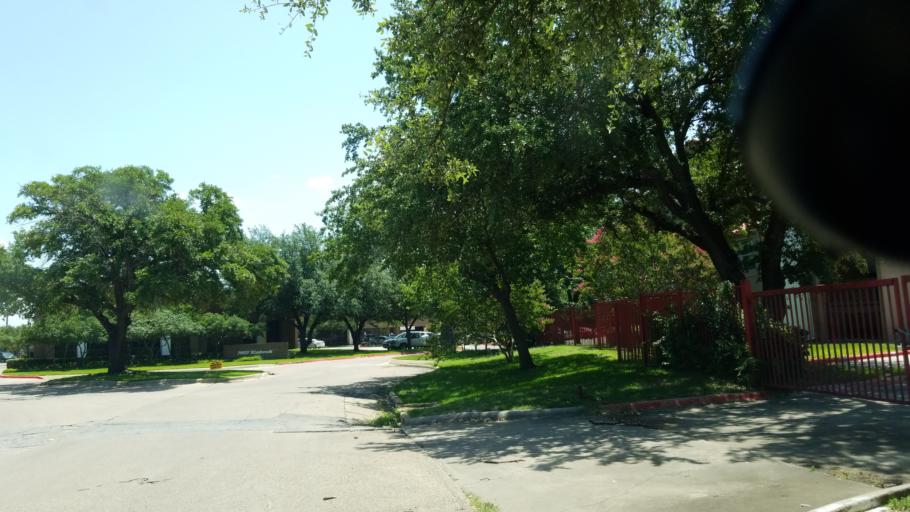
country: US
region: Texas
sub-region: Dallas County
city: Dallas
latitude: 32.8195
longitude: -96.8640
